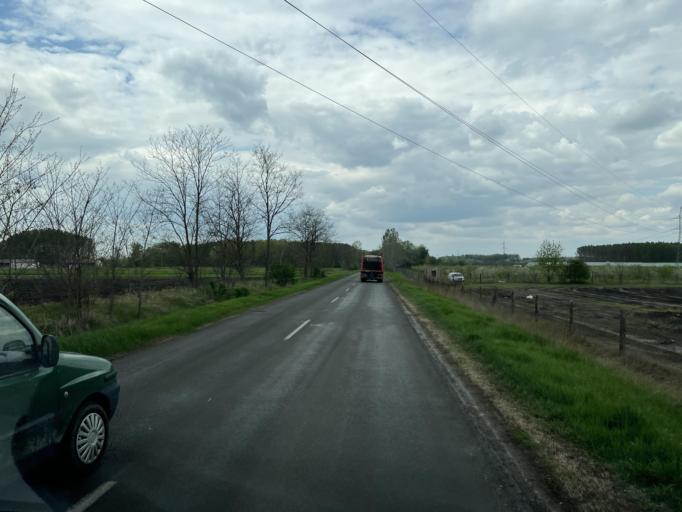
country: HU
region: Pest
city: Hernad
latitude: 47.1876
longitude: 19.4236
